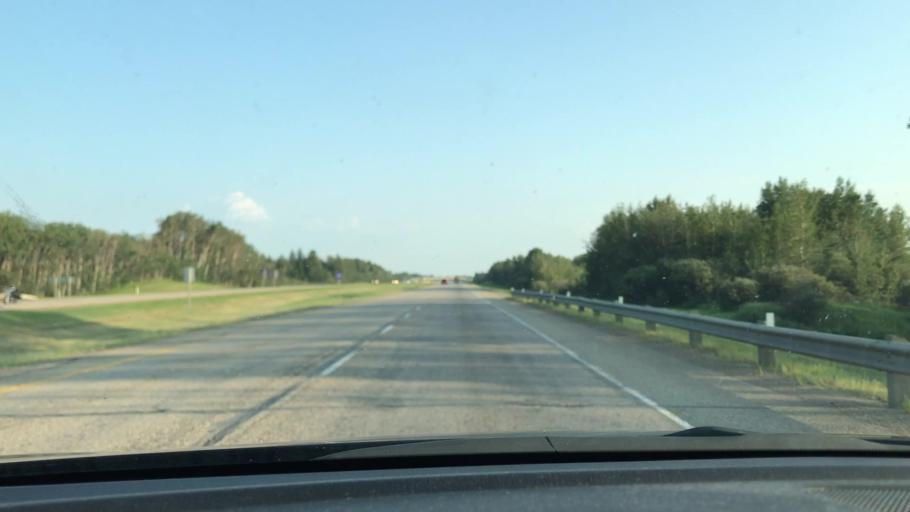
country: CA
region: Alberta
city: Lacombe
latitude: 52.5731
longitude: -113.6631
